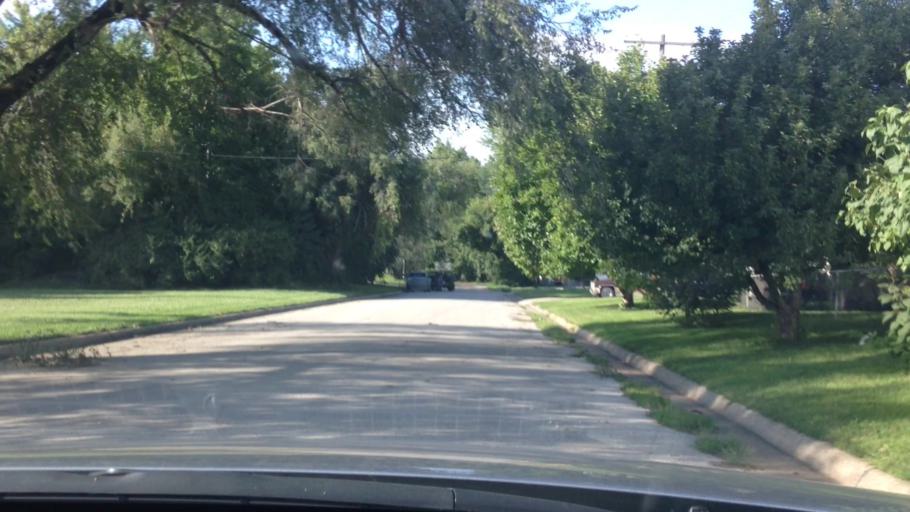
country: US
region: Kansas
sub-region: Leavenworth County
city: Leavenworth
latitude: 39.2906
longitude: -94.9090
